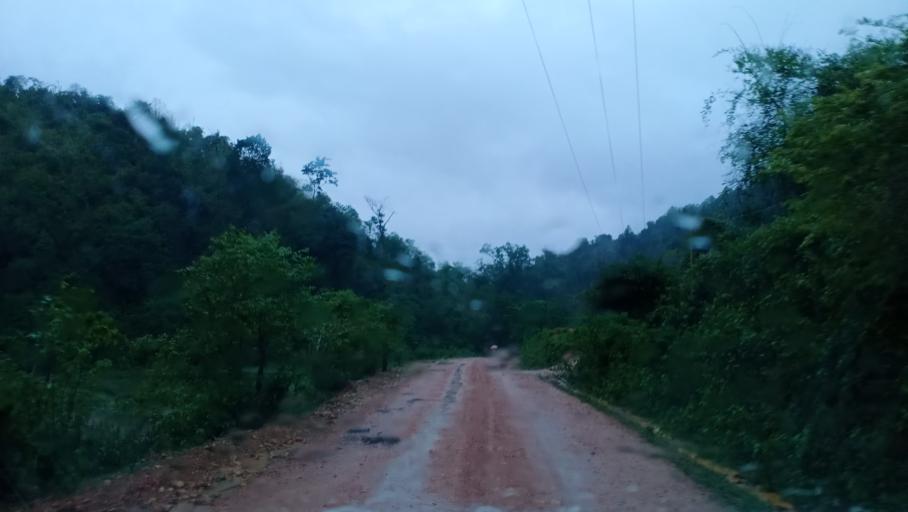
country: LA
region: Phongsali
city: Khoa
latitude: 21.1365
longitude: 102.3228
